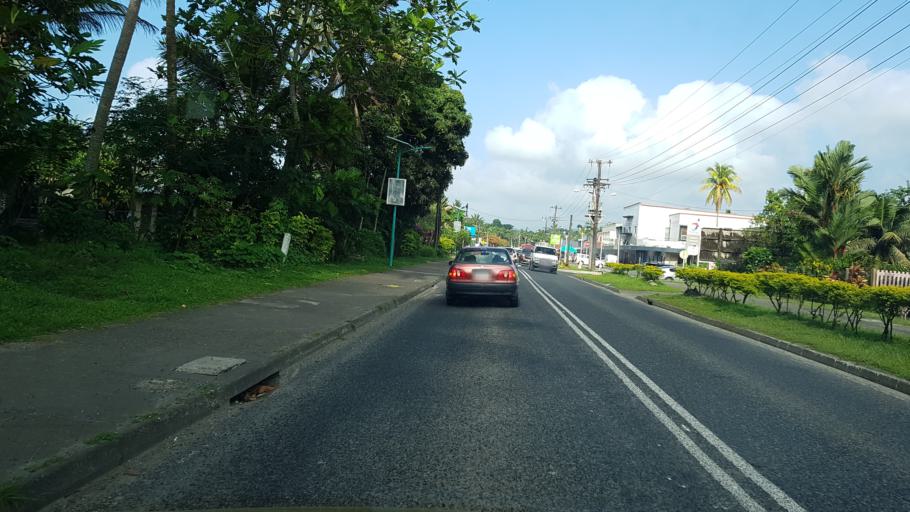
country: FJ
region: Central
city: Suva
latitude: -18.1139
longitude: 178.4083
